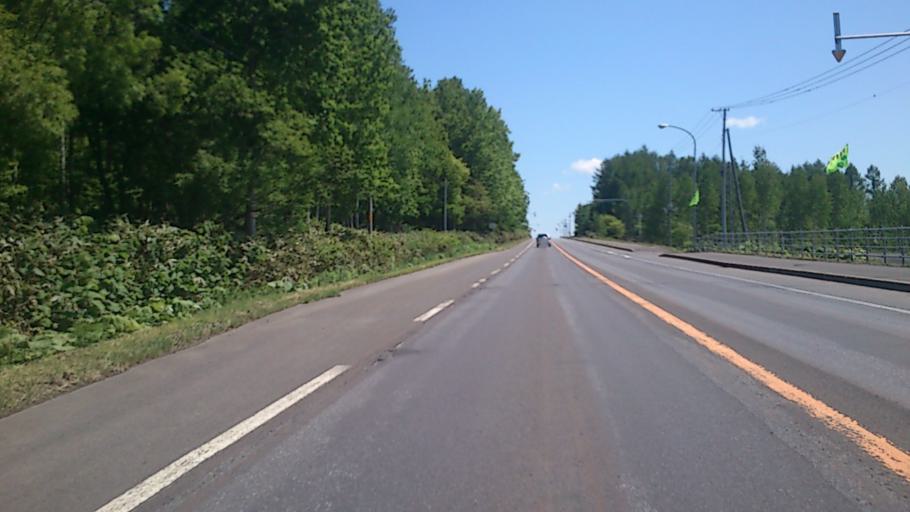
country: JP
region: Hokkaido
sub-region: Asahikawa-shi
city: Asahikawa
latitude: 44.0572
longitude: 142.4043
